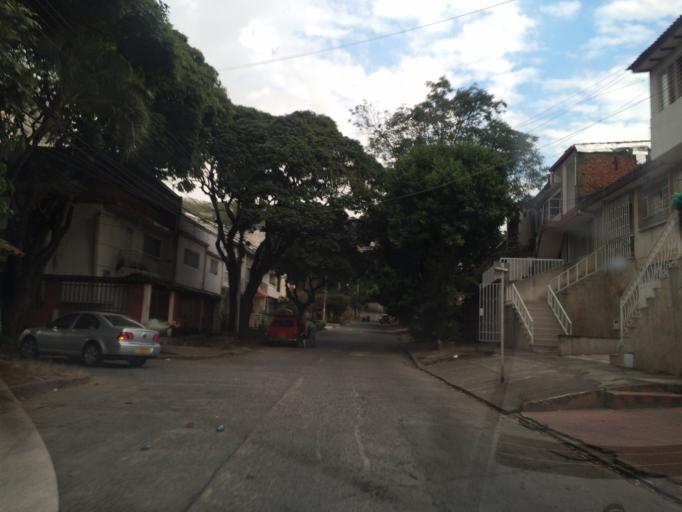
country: CO
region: Valle del Cauca
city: Cali
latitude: 3.4386
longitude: -76.5449
